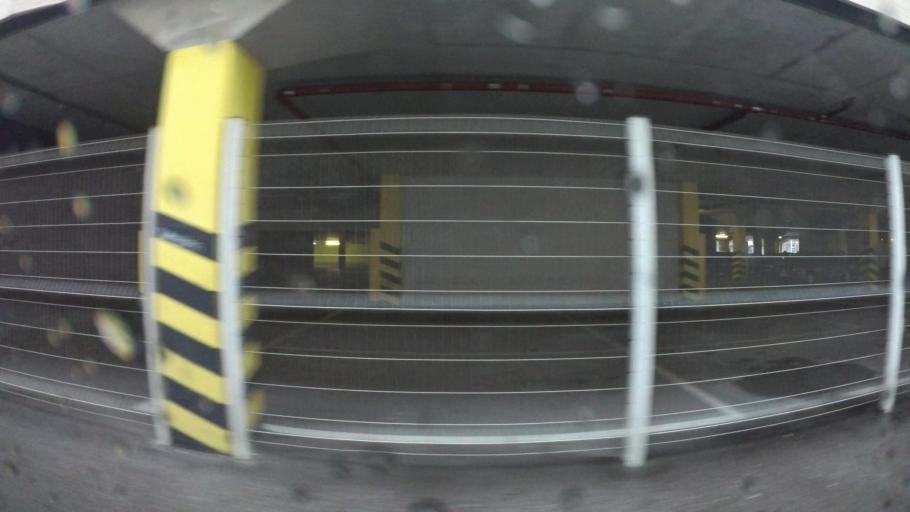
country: BA
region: Federation of Bosnia and Herzegovina
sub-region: Hercegovacko-Bosanski Kanton
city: Mostar
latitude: 43.3457
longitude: 17.7985
